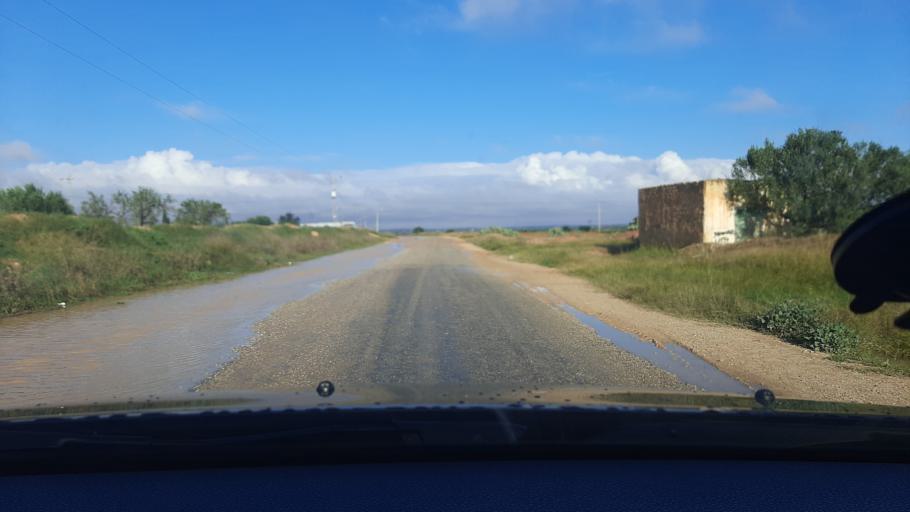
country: TN
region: Safaqis
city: Sfax
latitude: 34.8801
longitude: 10.6330
